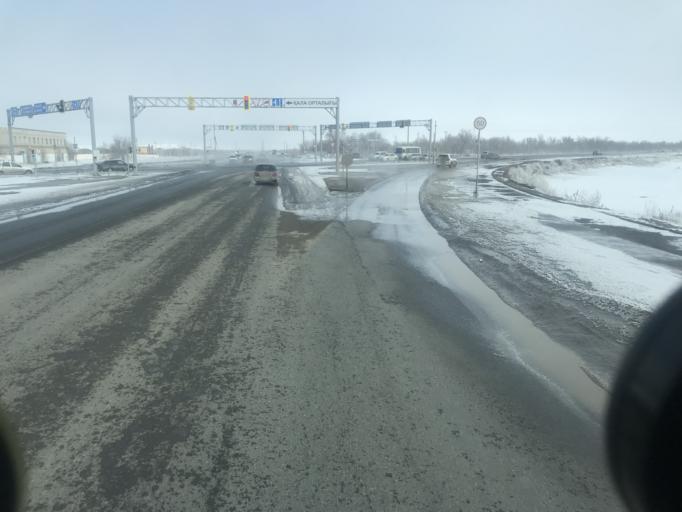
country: KZ
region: Aqtoebe
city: Aqtobe
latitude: 50.2898
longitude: 57.2892
